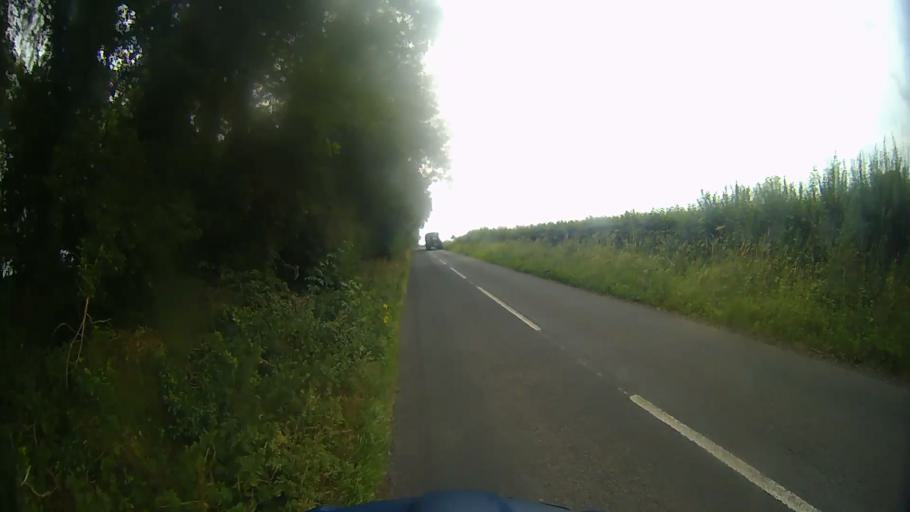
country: GB
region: England
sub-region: Hampshire
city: Kingsclere
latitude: 51.2906
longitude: -1.2689
